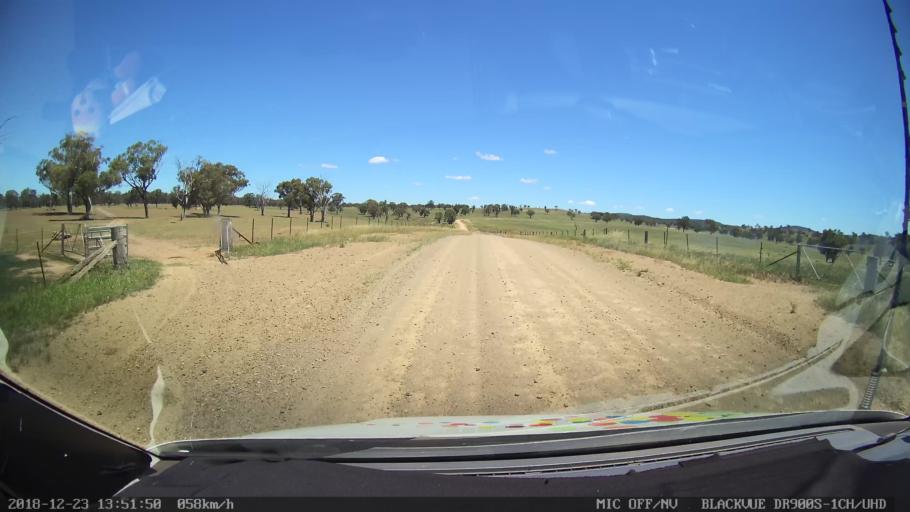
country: AU
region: New South Wales
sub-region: Tamworth Municipality
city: Manilla
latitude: -30.5432
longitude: 151.1046
